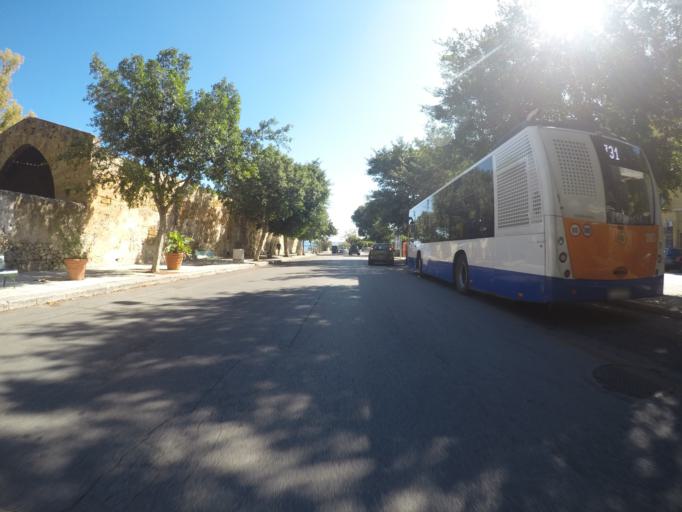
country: IT
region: Sicily
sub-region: Palermo
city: Palermo
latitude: 38.1655
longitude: 13.3681
